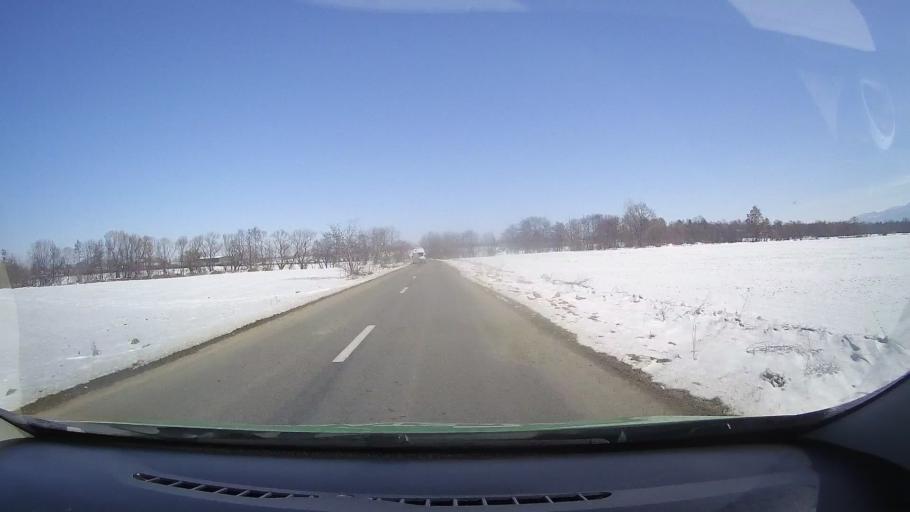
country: RO
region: Brasov
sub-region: Comuna Harseni
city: Harseni
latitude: 45.7332
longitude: 24.9995
